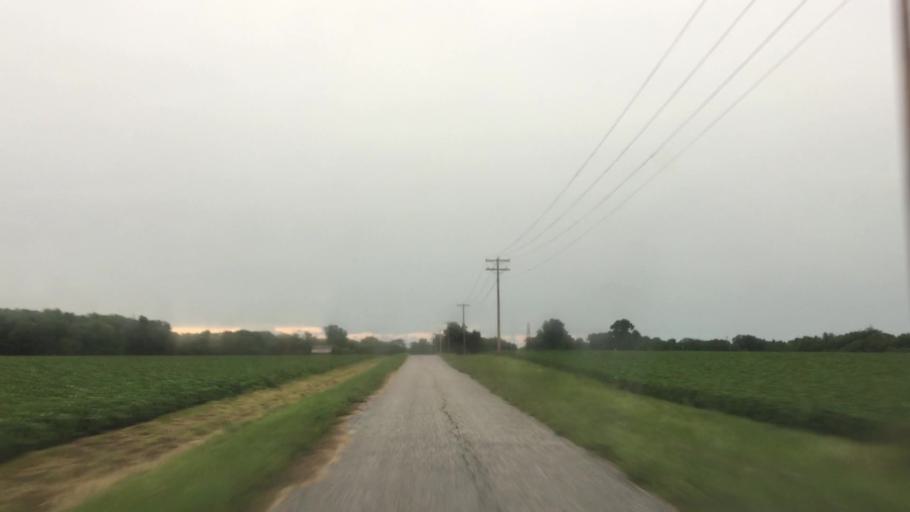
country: US
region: Illinois
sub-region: Hancock County
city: Nauvoo
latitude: 40.5494
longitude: -91.3592
